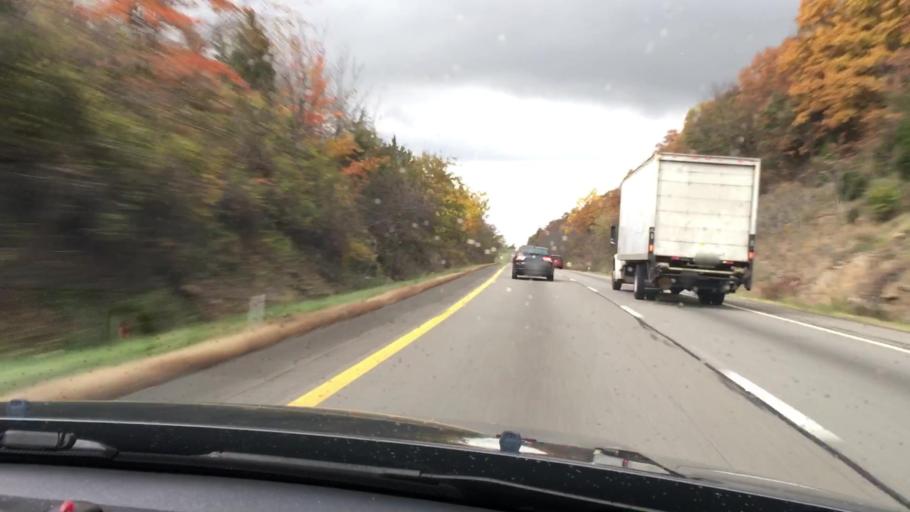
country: US
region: New York
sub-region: Dutchess County
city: Fishkill
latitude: 41.5301
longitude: -73.9250
